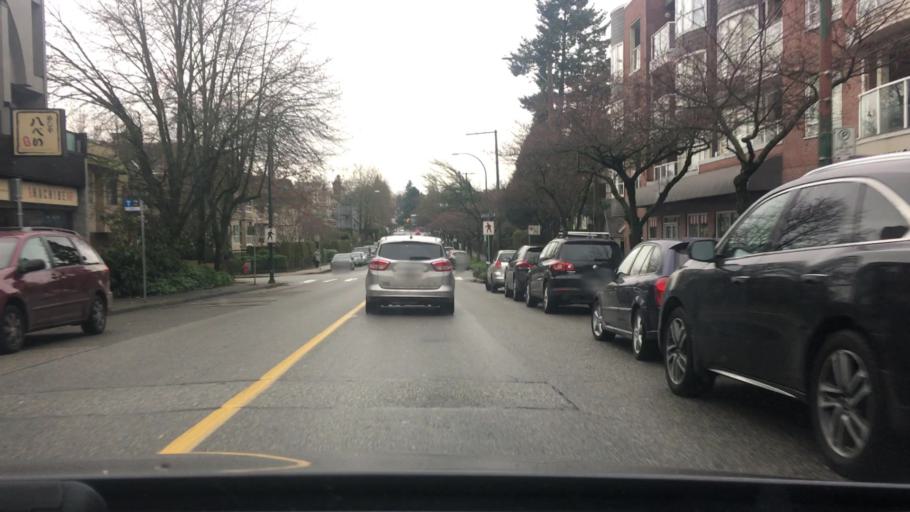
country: CA
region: British Columbia
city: Vancouver
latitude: 49.2570
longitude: -123.1212
